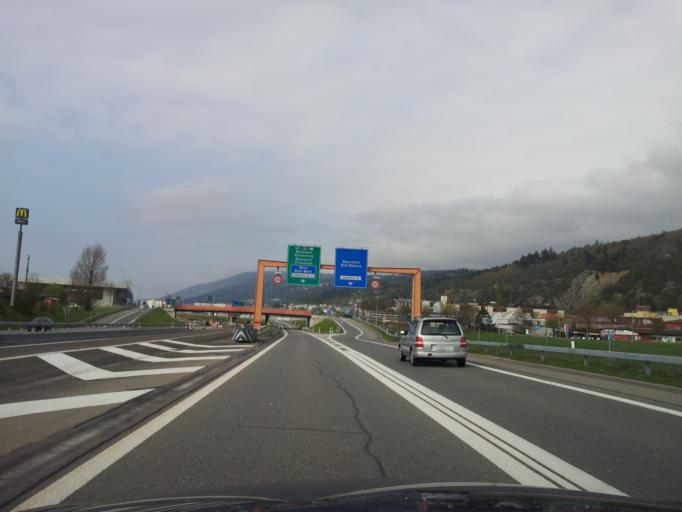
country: CH
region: Bern
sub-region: Biel/Bienne District
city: Orpund
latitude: 47.1599
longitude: 7.2893
